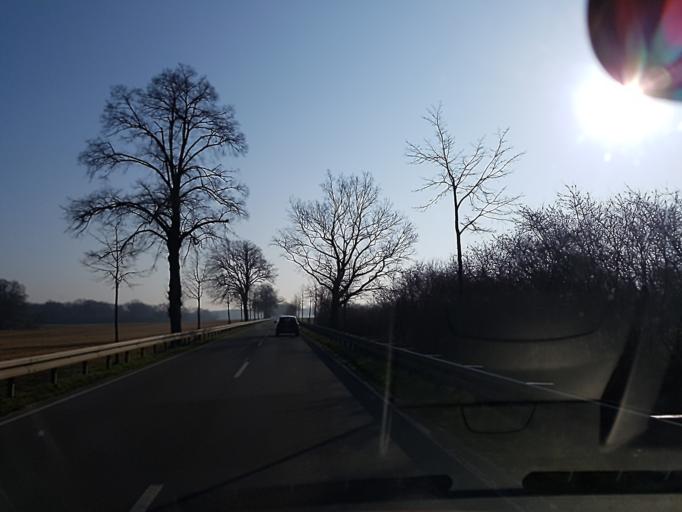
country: DE
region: Brandenburg
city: Calau
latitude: 51.7574
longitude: 13.9911
